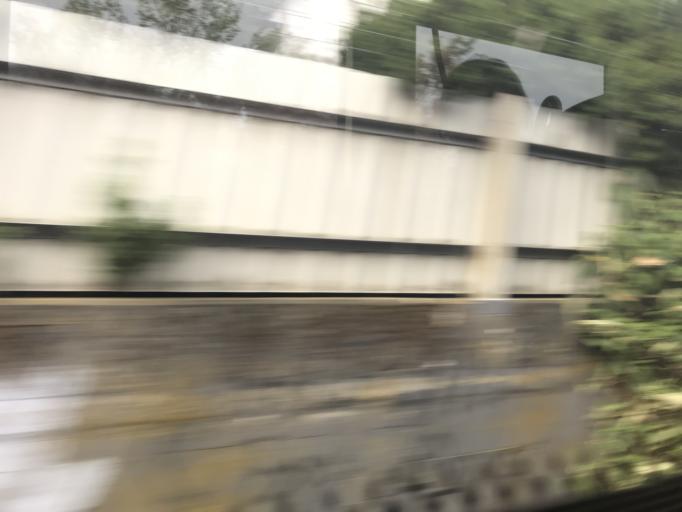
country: DE
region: Hesse
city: Kelkheim (Taunus)
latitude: 50.1226
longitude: 8.4662
